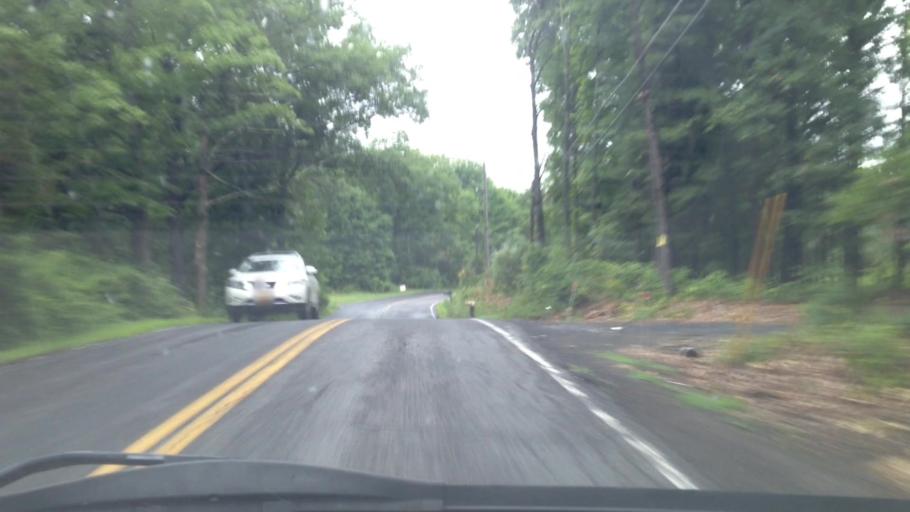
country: US
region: New York
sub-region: Ulster County
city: New Paltz
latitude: 41.7751
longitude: -74.0586
